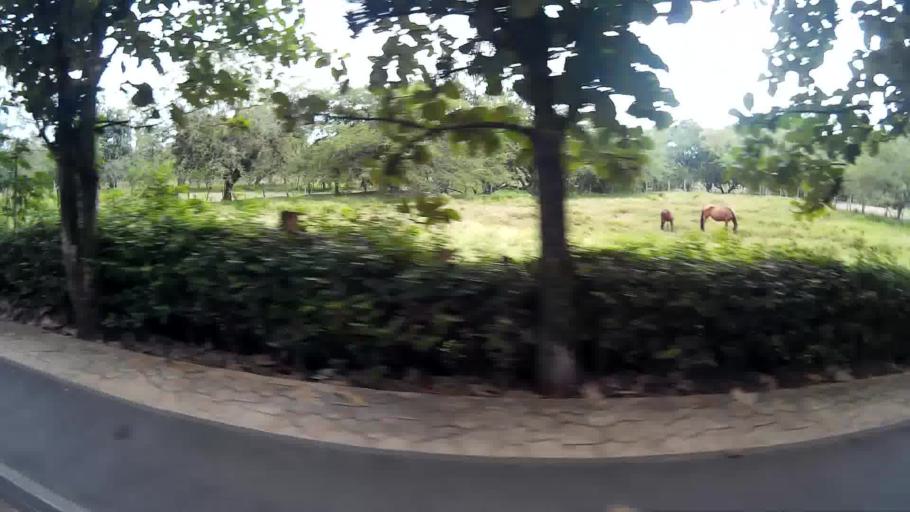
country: CO
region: Risaralda
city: La Virginia
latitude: 4.8914
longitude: -75.8765
